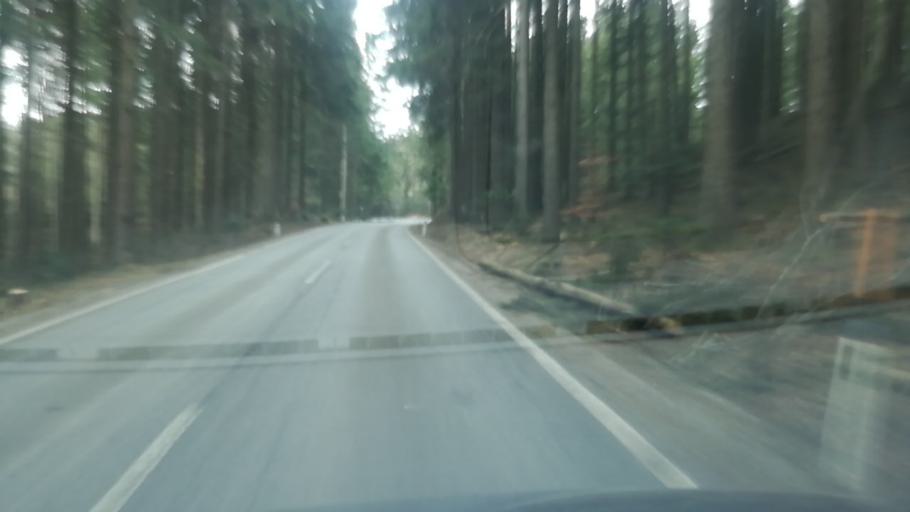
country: AT
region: Upper Austria
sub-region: Politischer Bezirk Vocklabruck
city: Frankenburg
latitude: 48.1096
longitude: 13.4848
